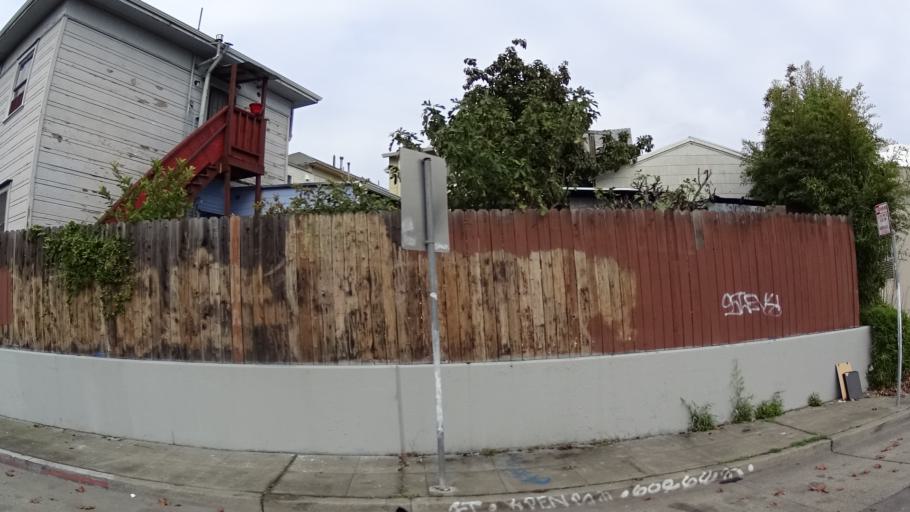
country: US
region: California
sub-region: Alameda County
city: Oakland
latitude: 37.7901
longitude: -122.2517
